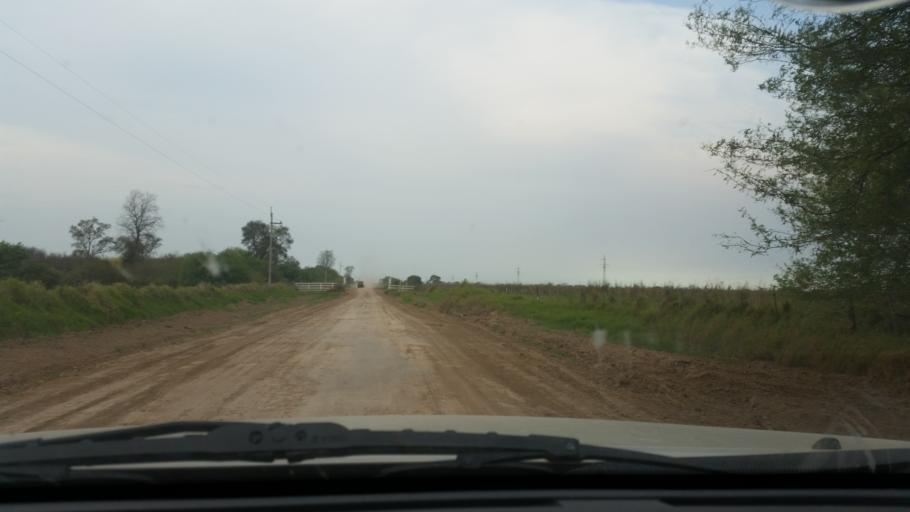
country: PY
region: Boqueron
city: Colonia Menno
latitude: -22.3558
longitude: -59.5704
